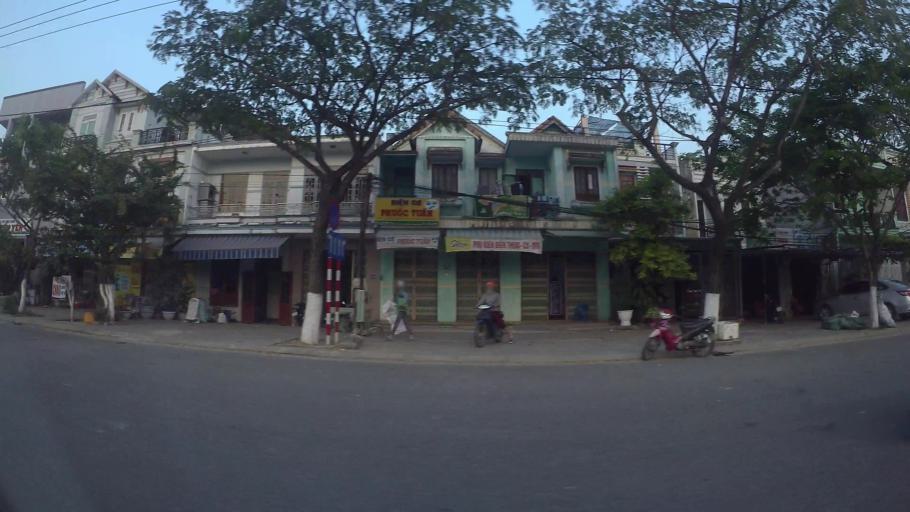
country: VN
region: Da Nang
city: Ngu Hanh Son
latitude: 15.9998
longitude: 108.2600
